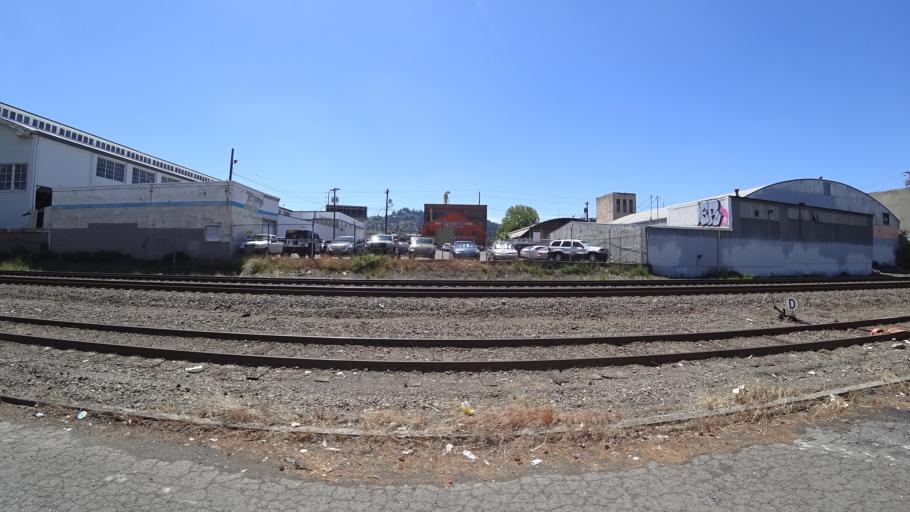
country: US
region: Oregon
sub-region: Multnomah County
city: Portland
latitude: 45.5424
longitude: -122.6974
